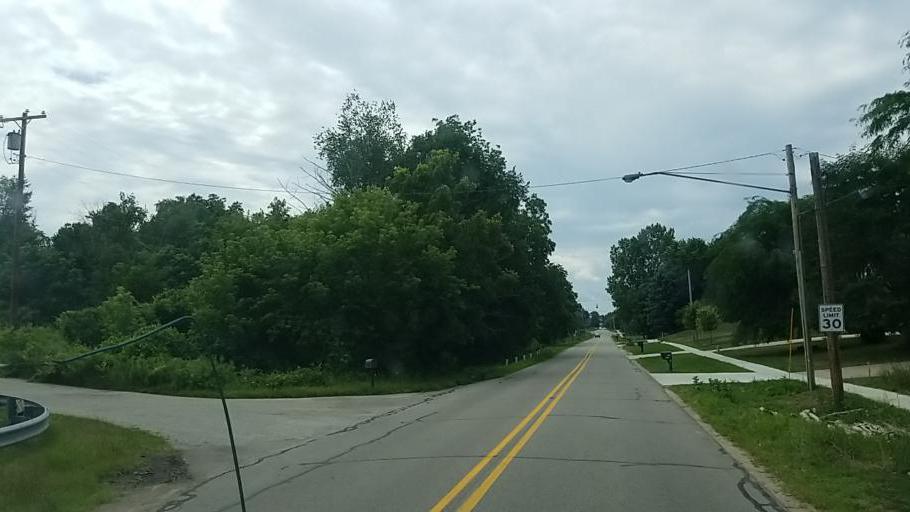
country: US
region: Michigan
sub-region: Kent County
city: Walker
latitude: 43.0009
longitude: -85.7382
